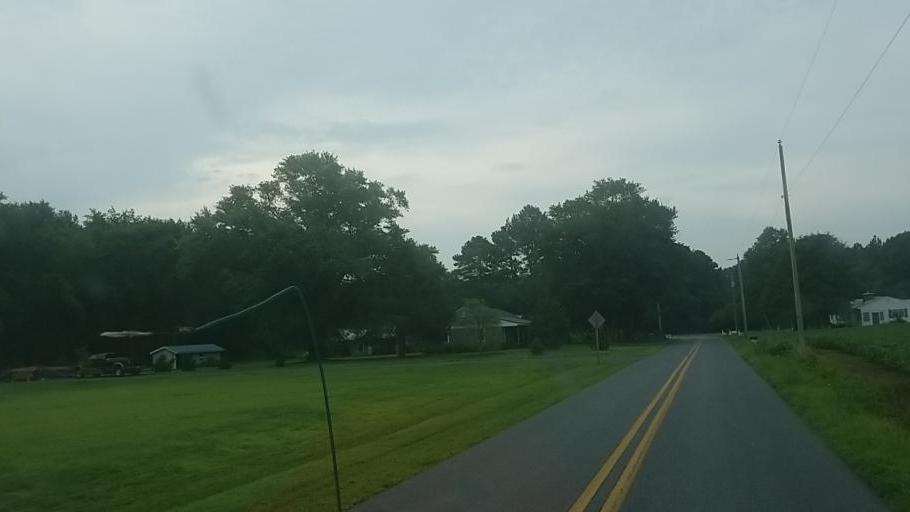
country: US
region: Delaware
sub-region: Sussex County
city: Selbyville
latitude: 38.4428
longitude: -75.2011
